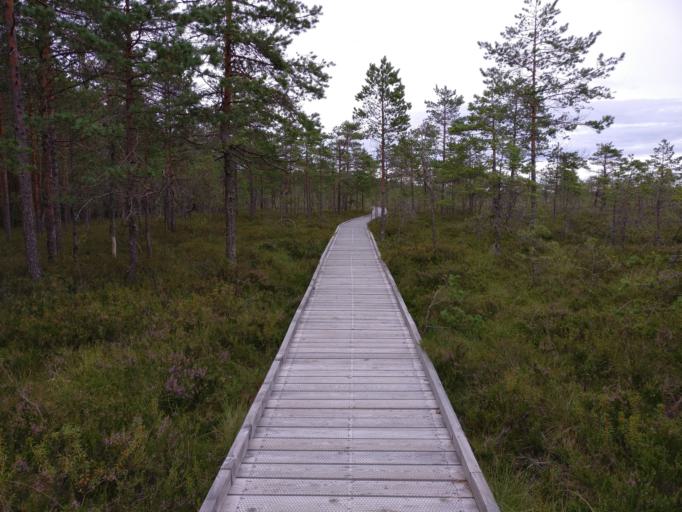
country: EE
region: Paernumaa
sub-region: Vaendra vald (alev)
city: Vandra
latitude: 58.4929
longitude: 24.9851
